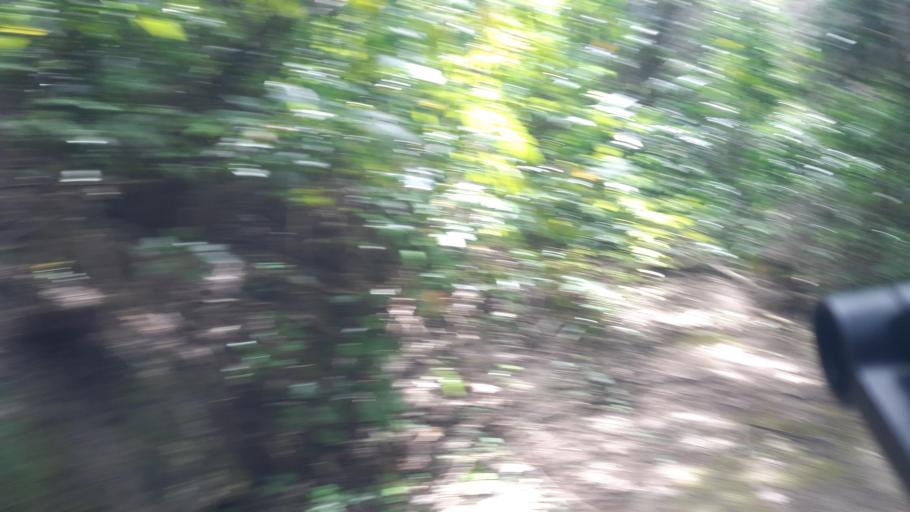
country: NZ
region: Marlborough
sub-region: Marlborough District
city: Picton
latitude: -41.2552
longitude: 174.0408
